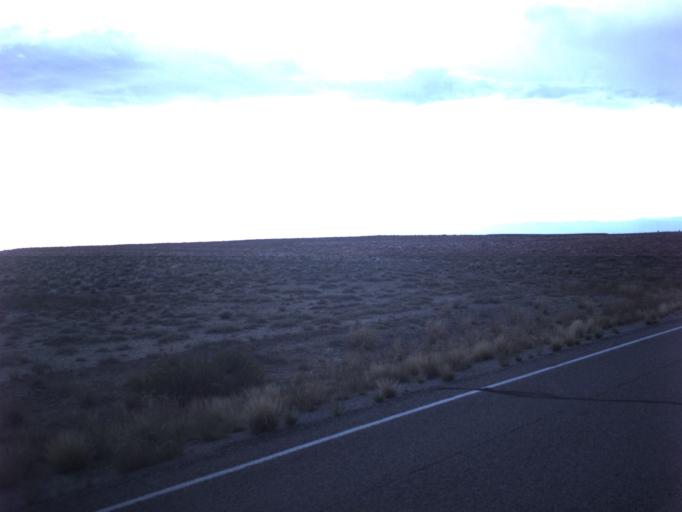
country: US
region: Utah
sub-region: Grand County
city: Moab
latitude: 38.9257
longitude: -109.3390
